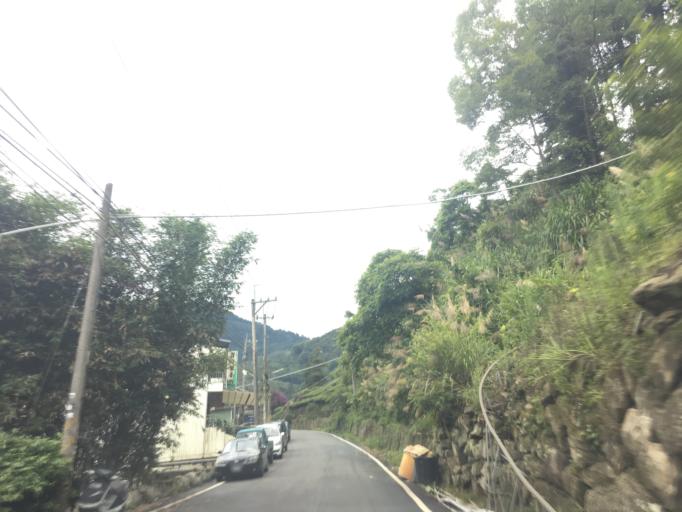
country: TW
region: Taiwan
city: Lugu
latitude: 23.5361
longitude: 120.7111
